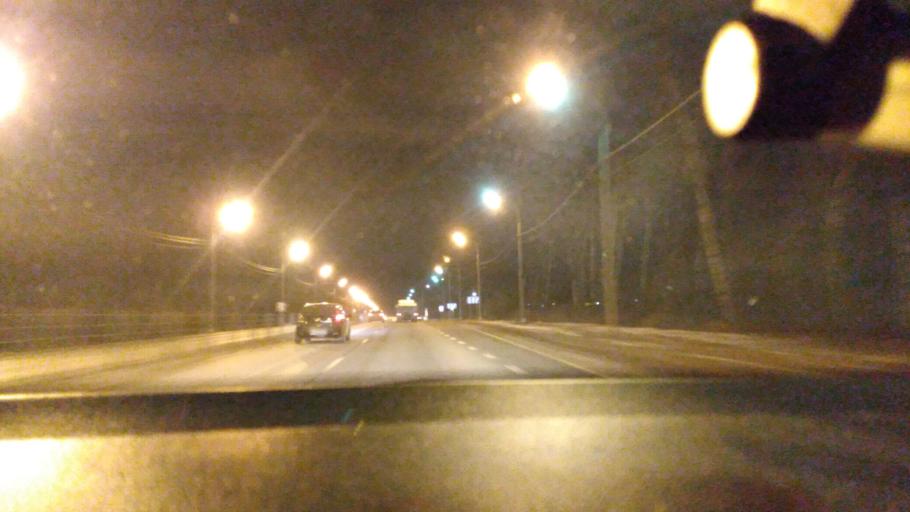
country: RU
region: Moskovskaya
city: Troitskoye
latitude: 55.2907
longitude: 38.4785
